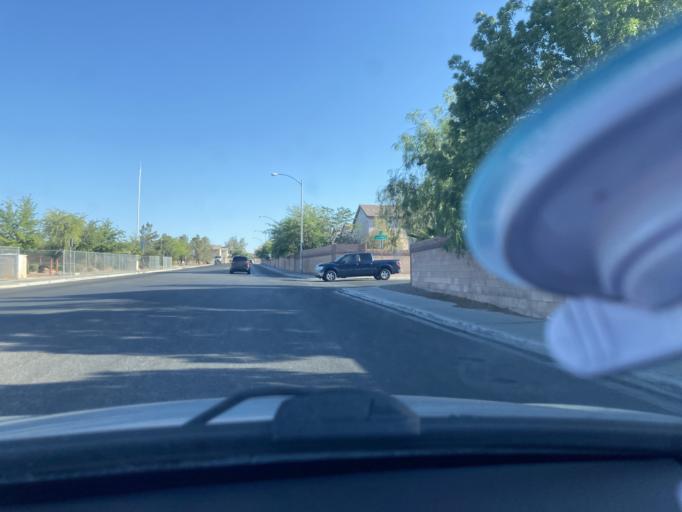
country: US
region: Nevada
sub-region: Clark County
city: Enterprise
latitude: 36.0614
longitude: -115.2930
